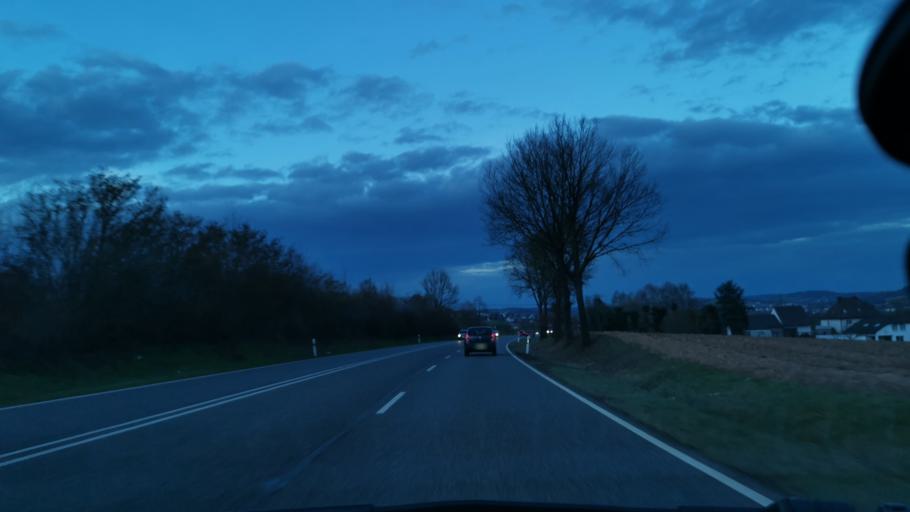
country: DE
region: Hesse
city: Breitenbach
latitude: 50.9419
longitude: 9.7716
